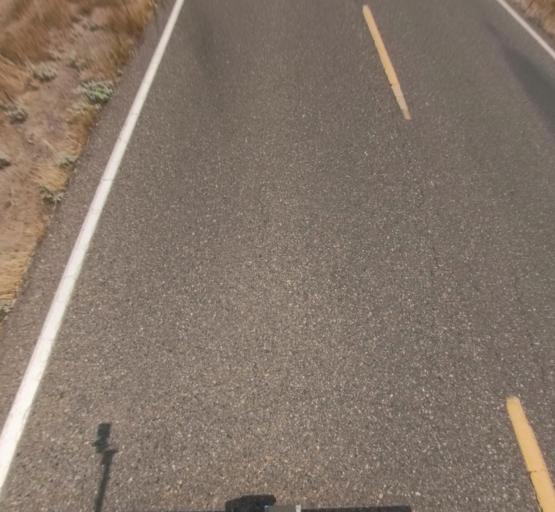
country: US
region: California
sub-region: Madera County
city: Madera Acres
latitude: 37.0583
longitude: -119.9825
